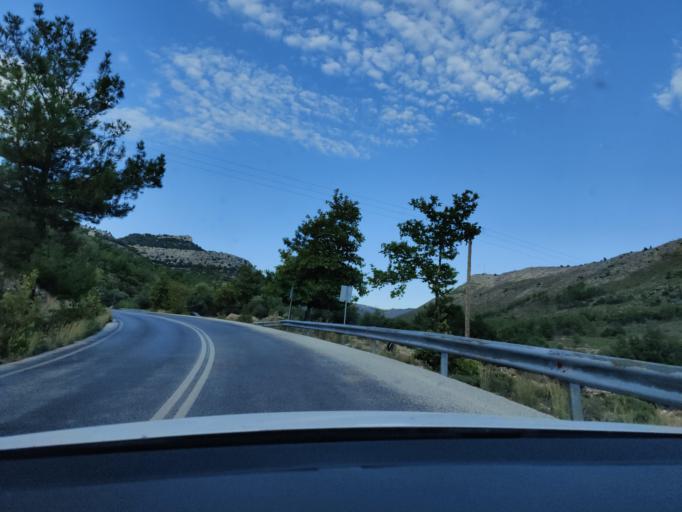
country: GR
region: East Macedonia and Thrace
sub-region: Nomos Kavalas
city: Limenaria
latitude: 40.6161
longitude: 24.6397
